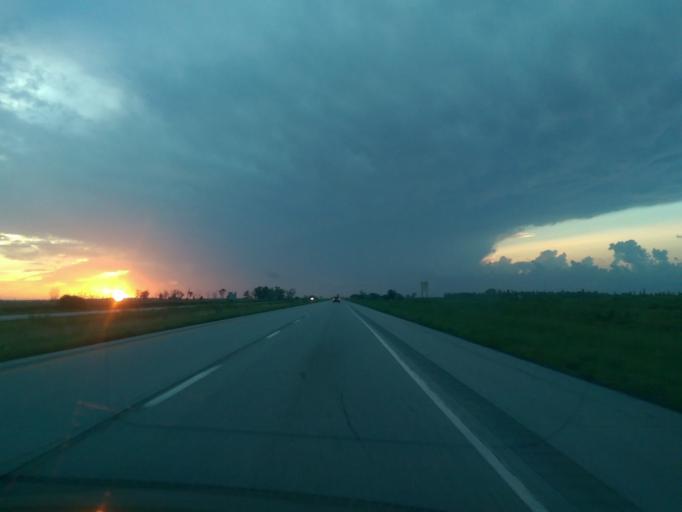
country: US
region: Iowa
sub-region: Fremont County
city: Hamburg
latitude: 40.6141
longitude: -95.6933
